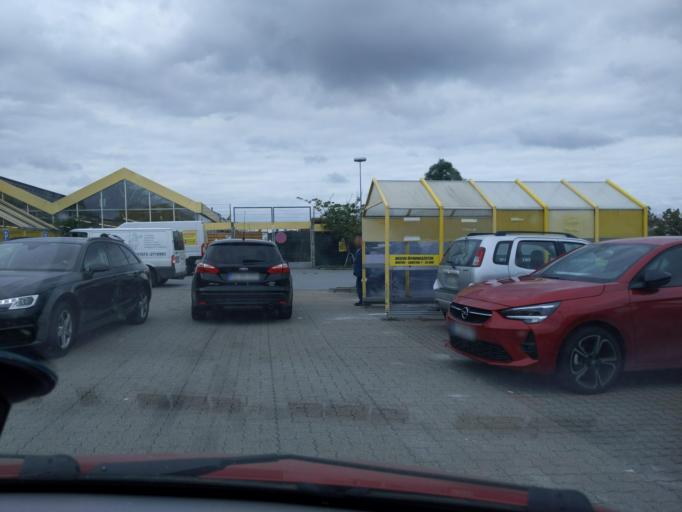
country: DE
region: Saxony
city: Bautzen
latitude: 51.1879
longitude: 14.4539
